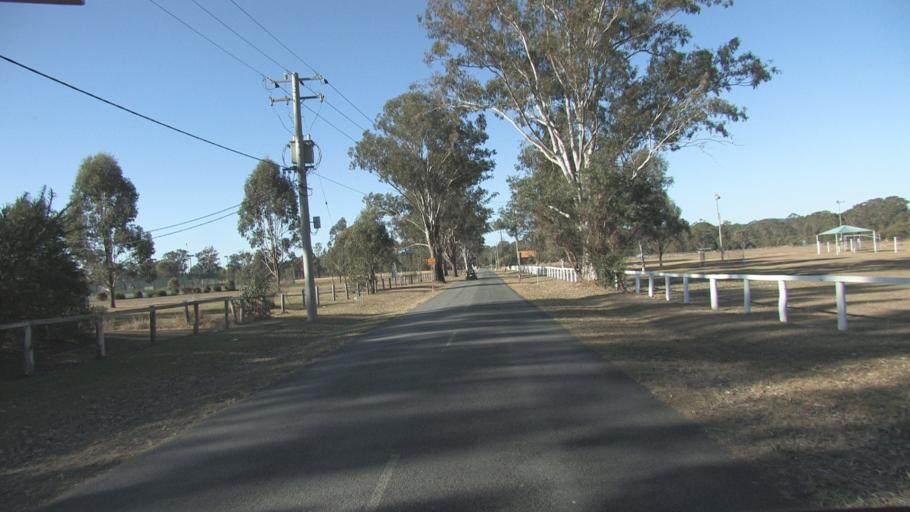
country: AU
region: Queensland
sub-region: Logan
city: Cedar Vale
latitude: -27.8305
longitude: 153.0088
